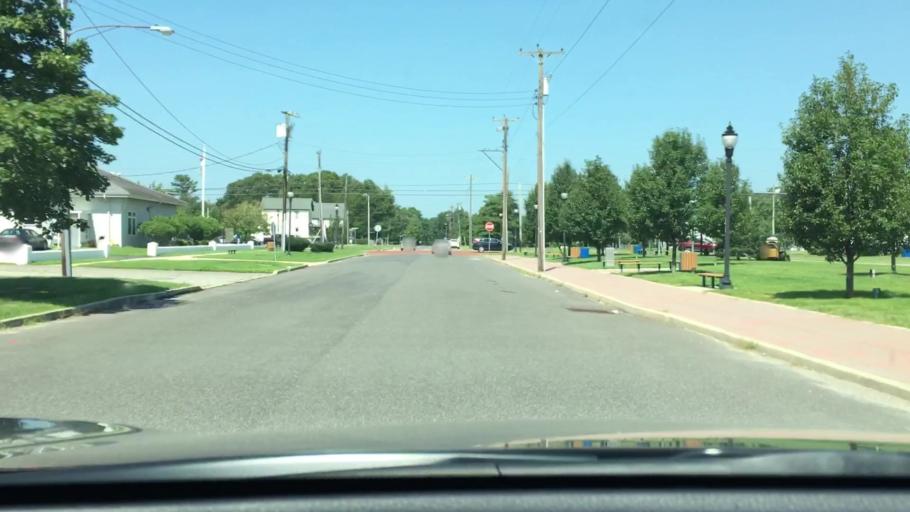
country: US
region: New Jersey
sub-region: Cape May County
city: Woodbine
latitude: 39.2410
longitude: -74.8148
